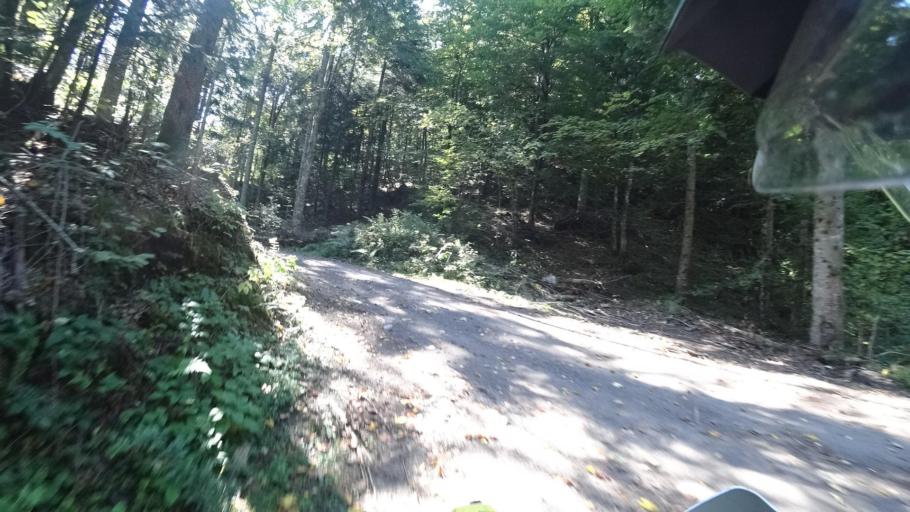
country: HR
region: Karlovacka
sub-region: Grad Ogulin
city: Ogulin
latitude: 45.2566
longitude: 15.1162
